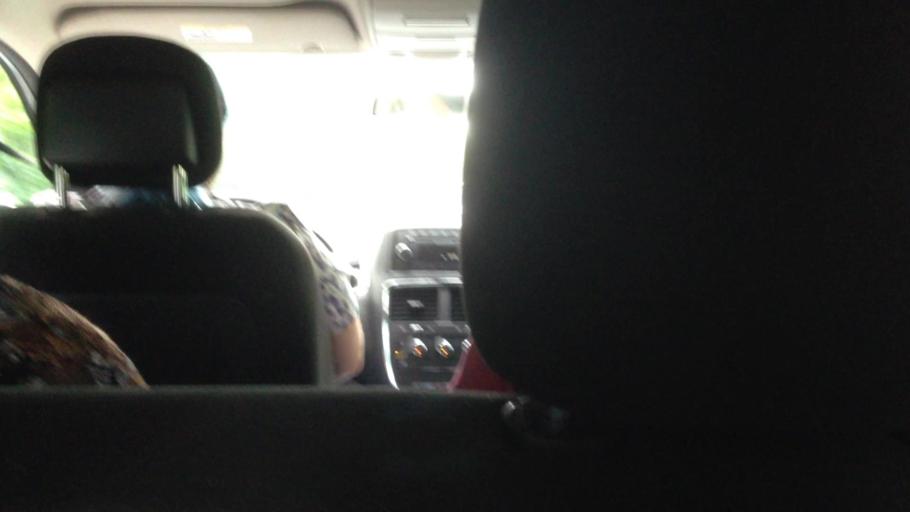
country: US
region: New York
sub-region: Dutchess County
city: Red Hook
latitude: 41.9826
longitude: -73.9105
